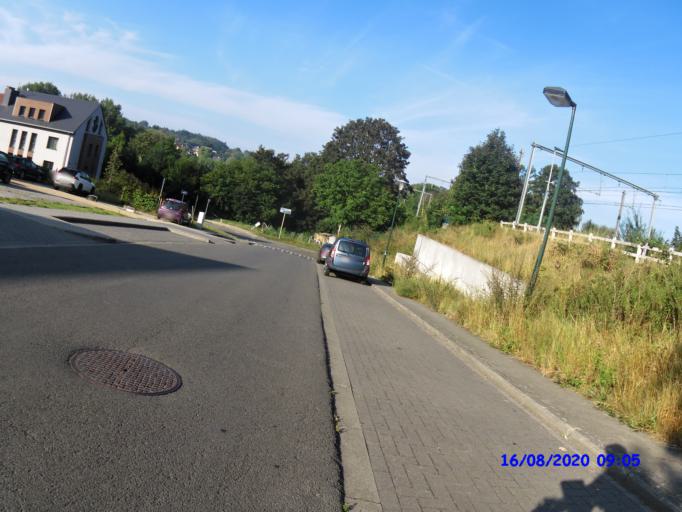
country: BE
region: Flanders
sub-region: Provincie Vlaams-Brabant
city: Linkebeek
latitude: 50.7784
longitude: 4.3314
